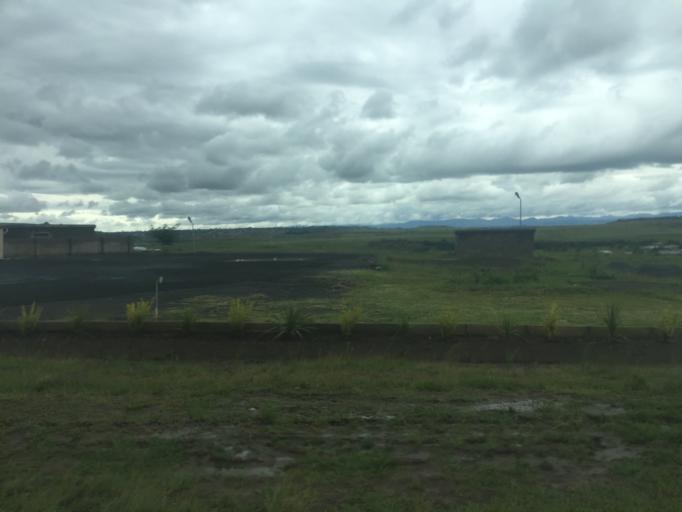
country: LS
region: Maseru
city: Maseru
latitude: -29.3881
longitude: 27.4703
